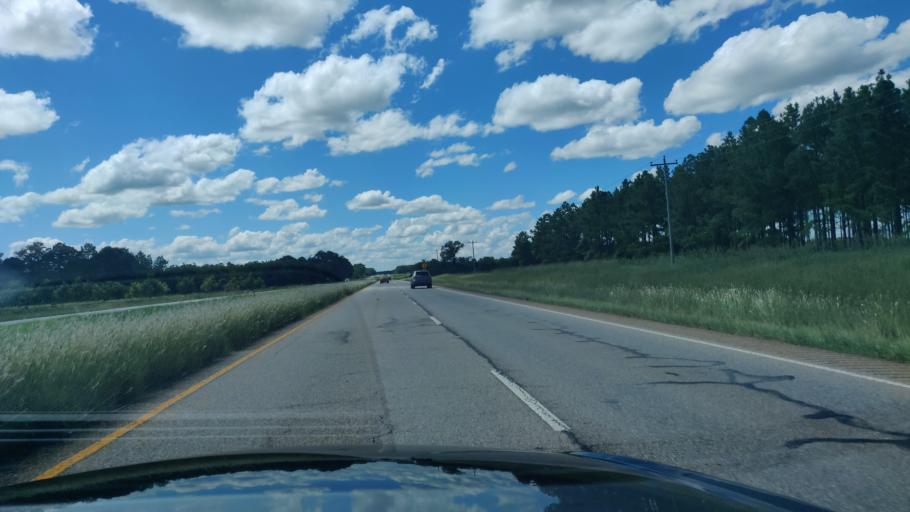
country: US
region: Georgia
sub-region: Webster County
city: Preston
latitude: 31.9483
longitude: -84.5768
